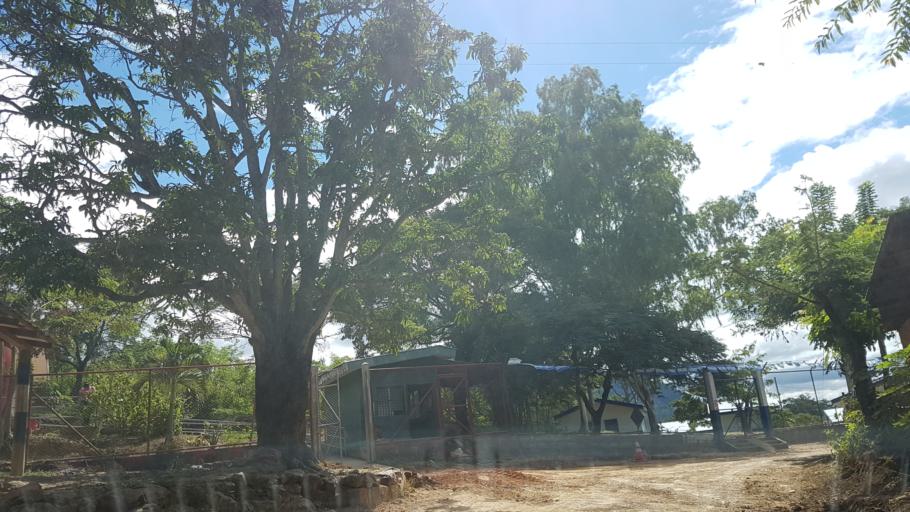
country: HN
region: El Paraiso
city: Santa Cruz
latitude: 13.7360
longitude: -86.6729
